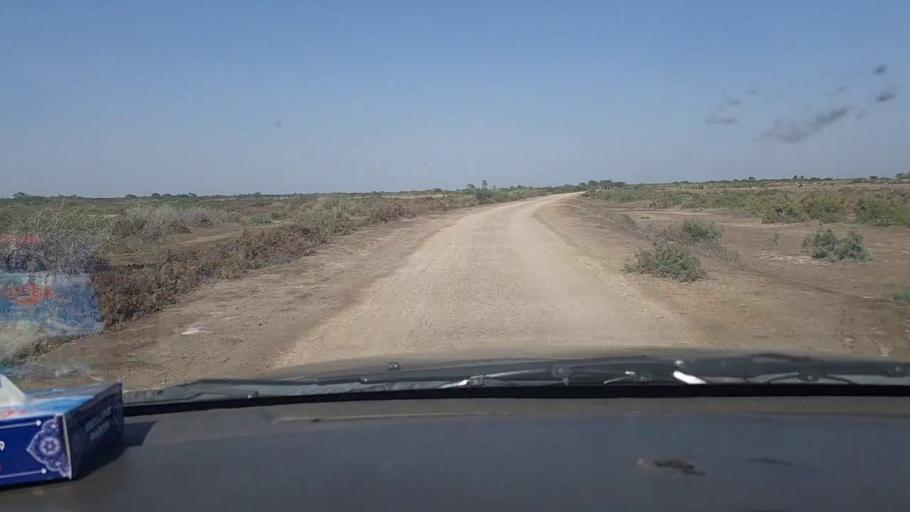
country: PK
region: Sindh
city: Chuhar Jamali
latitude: 24.2740
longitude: 67.7593
